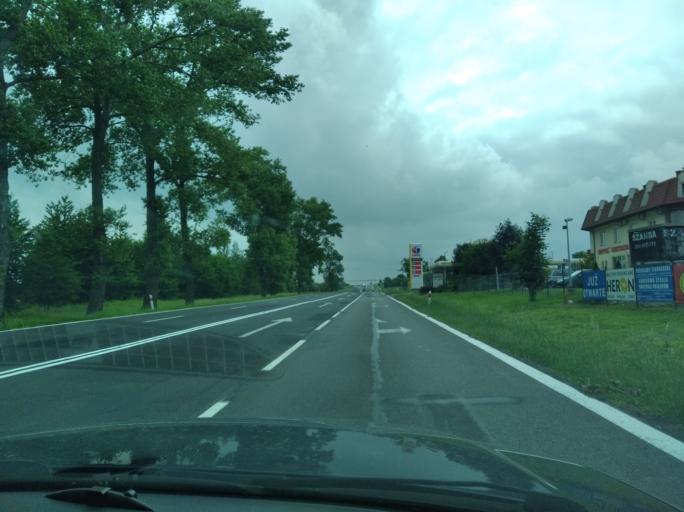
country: PL
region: Subcarpathian Voivodeship
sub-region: Powiat przeworski
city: Rozborz
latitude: 50.0509
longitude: 22.5253
